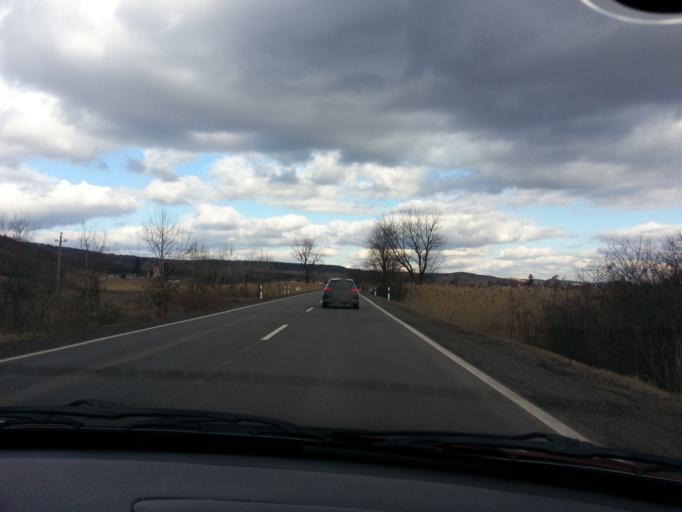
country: HU
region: Nograd
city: Matraverebely
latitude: 47.9681
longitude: 19.7637
